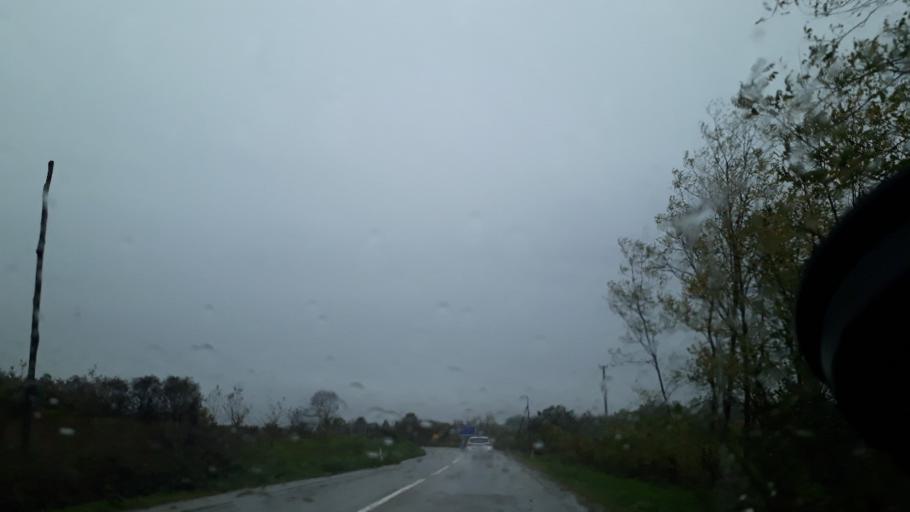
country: BA
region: Republika Srpska
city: Maglajani
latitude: 44.8652
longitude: 17.4305
